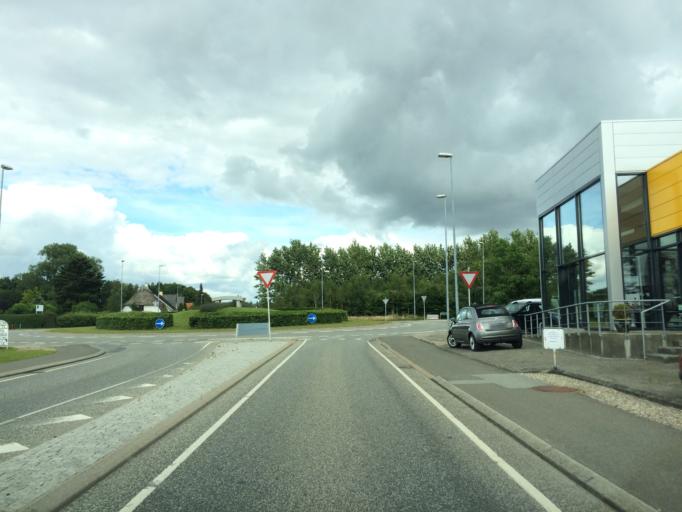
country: DK
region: South Denmark
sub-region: Assens Kommune
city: Tommerup
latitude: 55.2538
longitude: 10.2387
